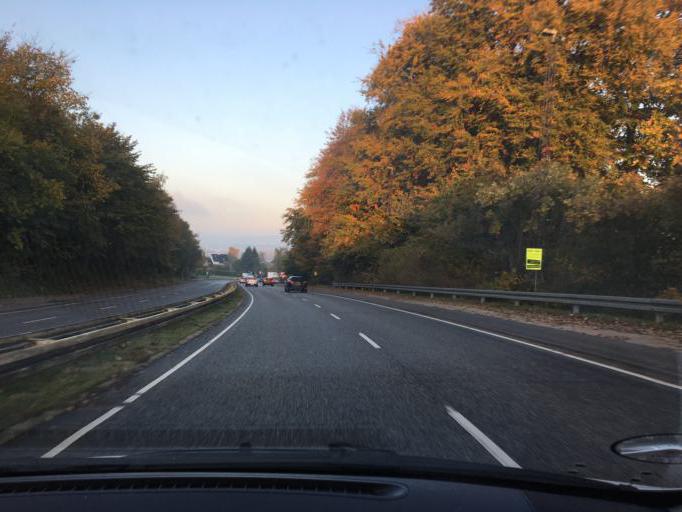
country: DK
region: South Denmark
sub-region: Vejle Kommune
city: Vejle
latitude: 55.7006
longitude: 9.5286
